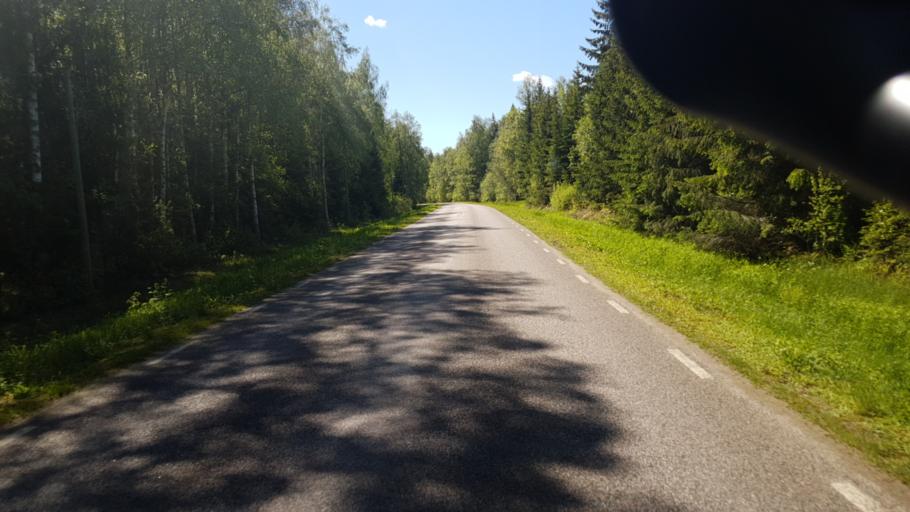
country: SE
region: Vaermland
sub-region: Grums Kommun
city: Slottsbron
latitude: 59.4873
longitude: 12.8829
